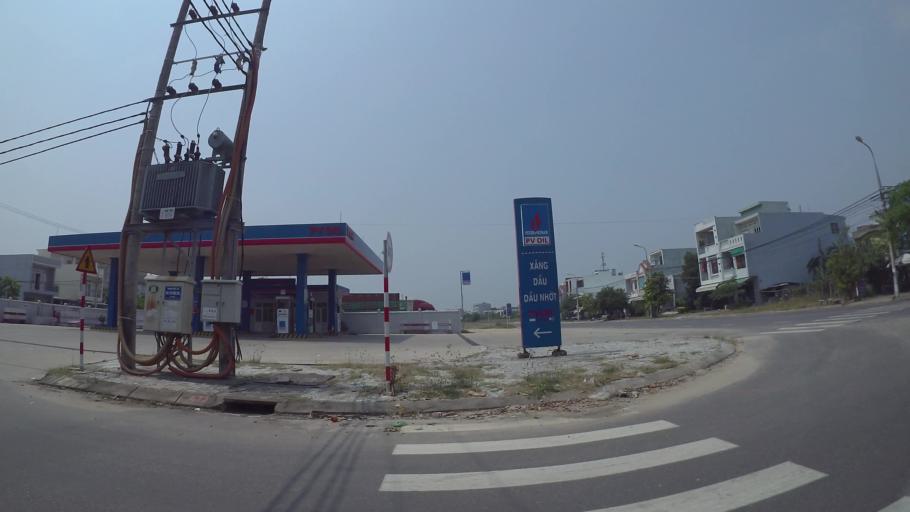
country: VN
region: Da Nang
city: Cam Le
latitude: 16.0034
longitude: 108.2176
